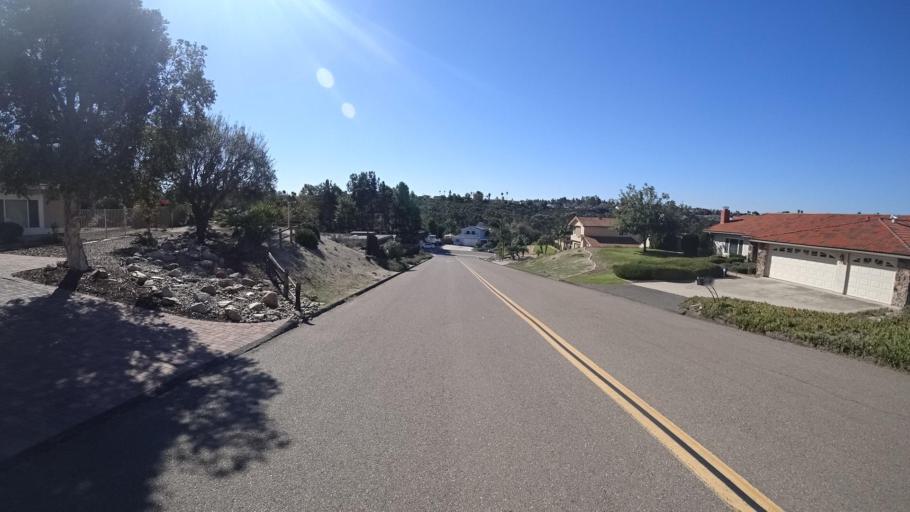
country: US
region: California
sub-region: San Diego County
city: Bonita
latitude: 32.6601
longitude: -117.0152
